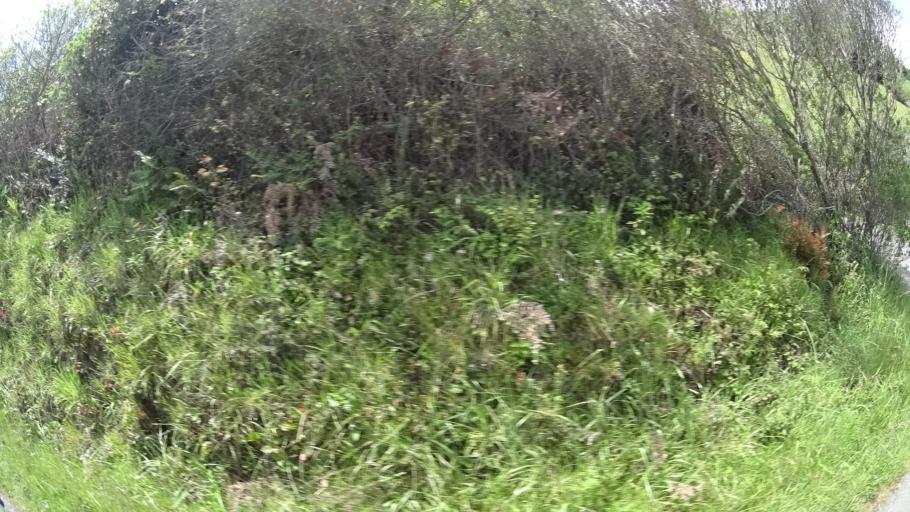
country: US
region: California
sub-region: Humboldt County
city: Humboldt Hill
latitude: 40.6778
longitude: -124.2274
